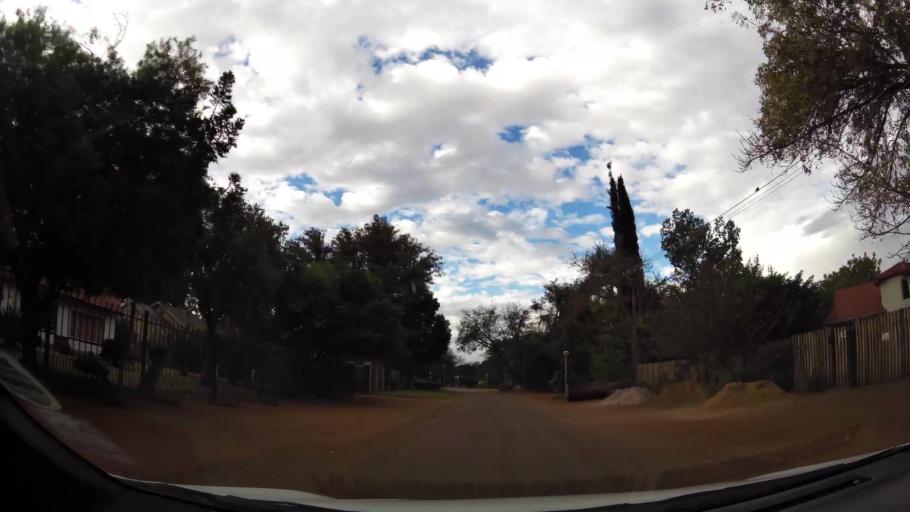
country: ZA
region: Limpopo
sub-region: Waterberg District Municipality
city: Modimolle
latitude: -24.5124
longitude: 28.7114
